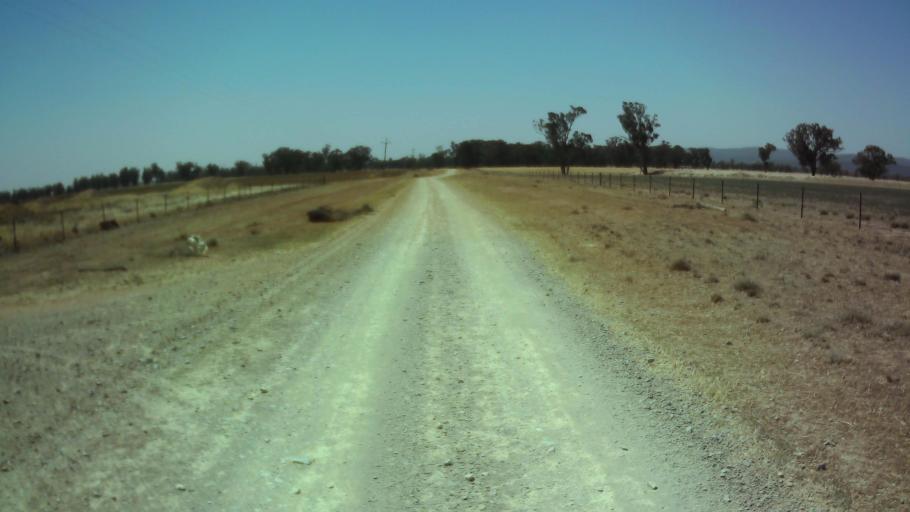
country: AU
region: New South Wales
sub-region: Weddin
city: Grenfell
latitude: -34.0250
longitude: 147.9006
